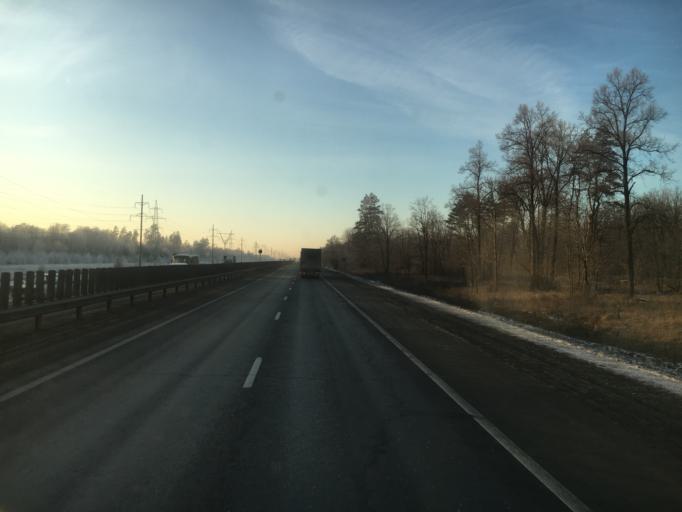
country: RU
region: Samara
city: Pribrezhnyy
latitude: 53.5162
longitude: 49.8624
